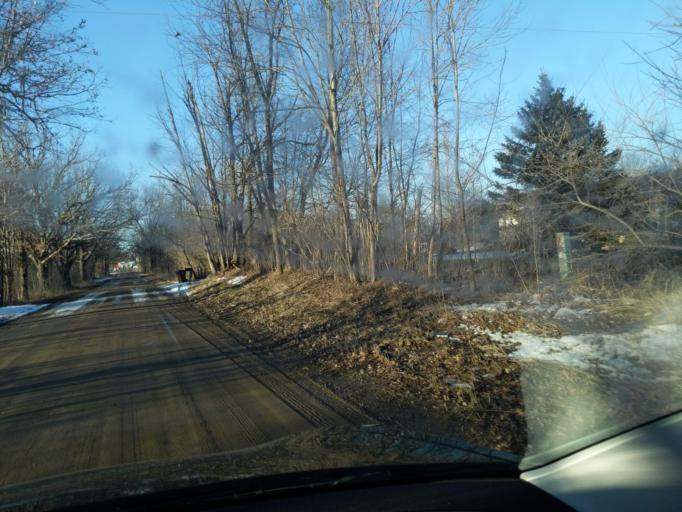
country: US
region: Michigan
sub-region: Ingham County
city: Stockbridge
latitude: 42.5058
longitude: -84.2412
